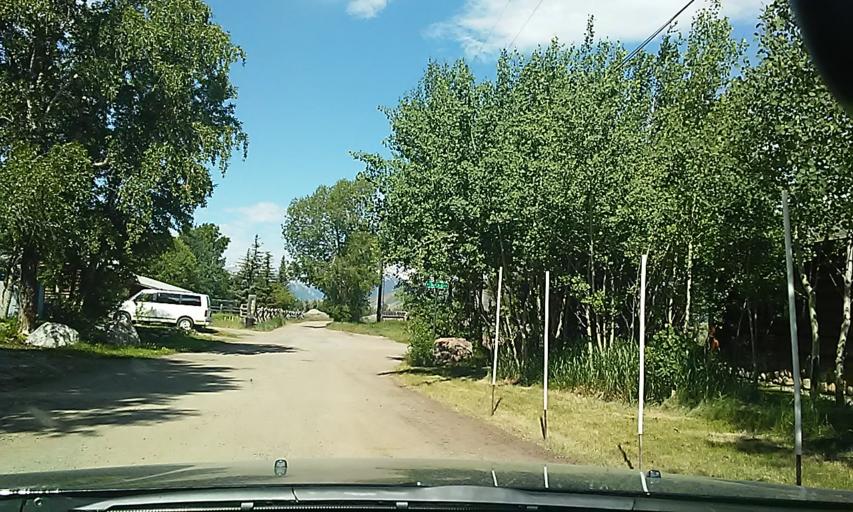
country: US
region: Wyoming
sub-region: Teton County
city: Jackson
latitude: 43.6216
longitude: -110.6273
